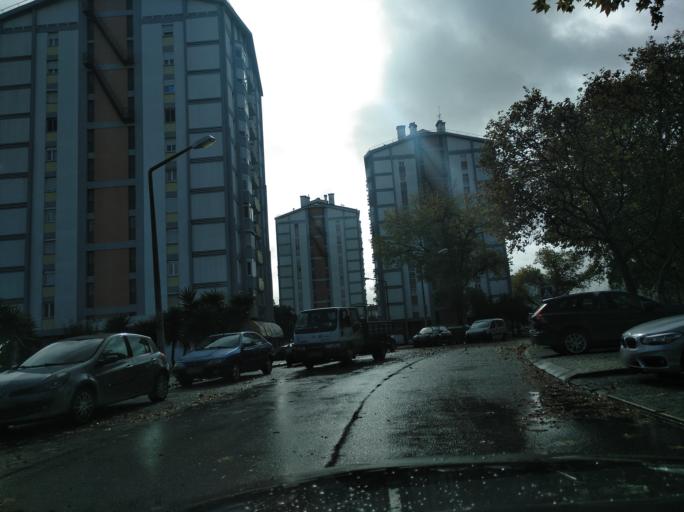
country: PT
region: Lisbon
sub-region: Loures
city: Moscavide
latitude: 38.7595
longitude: -9.1075
